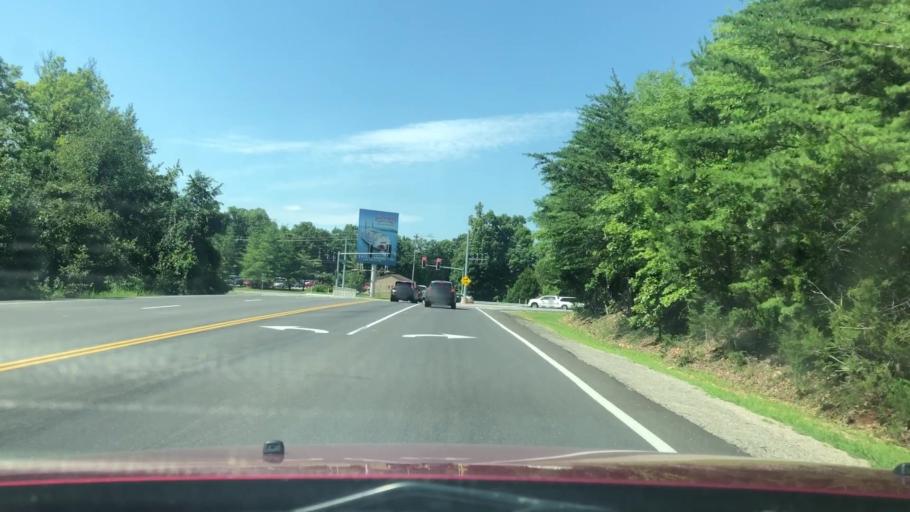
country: US
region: Missouri
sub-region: Stone County
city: Kimberling City
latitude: 36.6702
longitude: -93.3350
